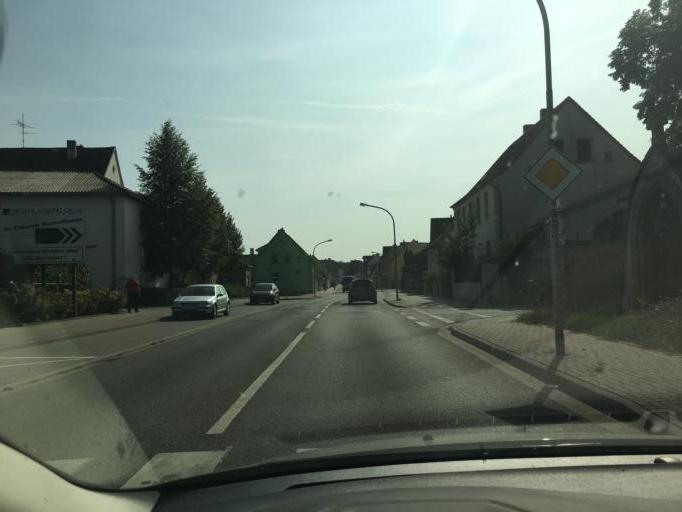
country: DE
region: Saxony-Anhalt
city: Calbe
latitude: 51.9081
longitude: 11.7738
